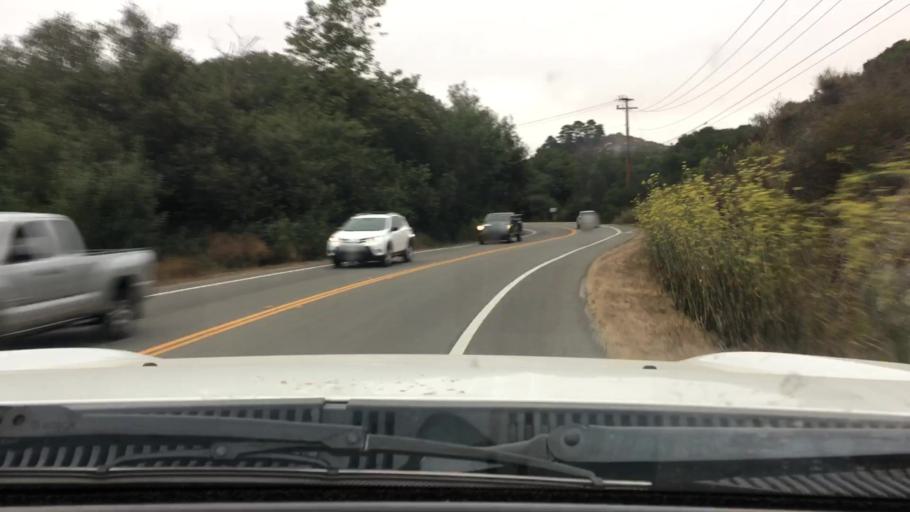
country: US
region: California
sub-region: San Luis Obispo County
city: Morro Bay
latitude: 35.3459
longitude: -120.8273
